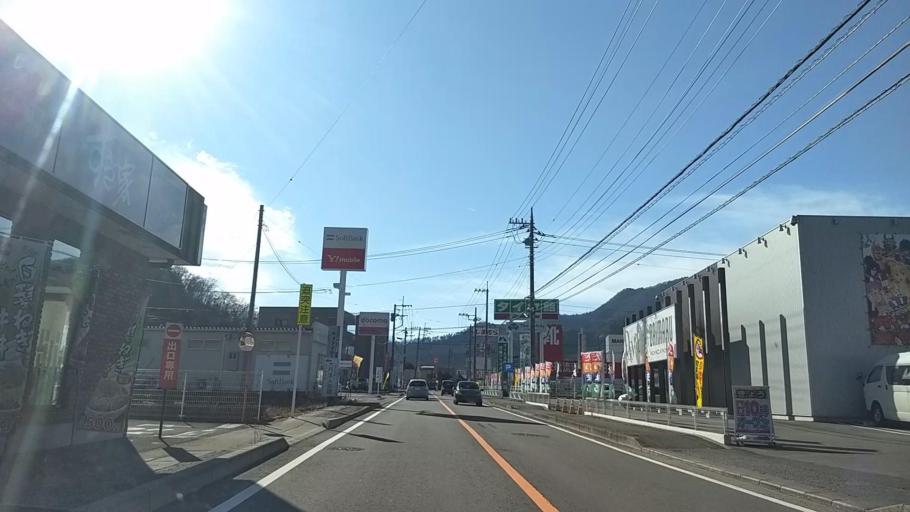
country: JP
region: Yamanashi
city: Otsuki
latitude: 35.6019
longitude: 138.9370
